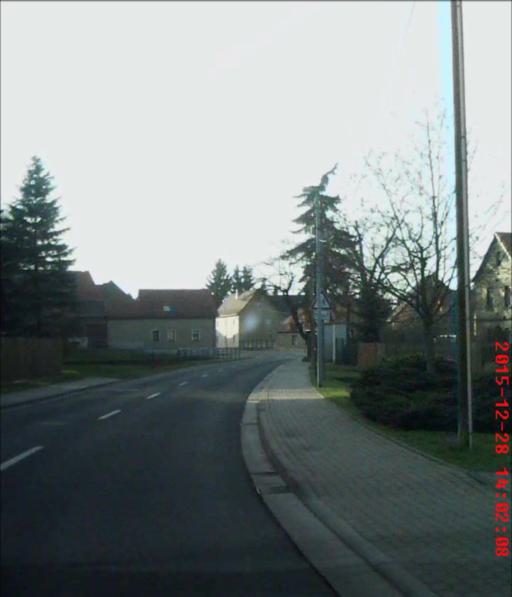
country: DE
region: Thuringia
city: Eberstedt
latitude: 51.0642
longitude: 11.5746
